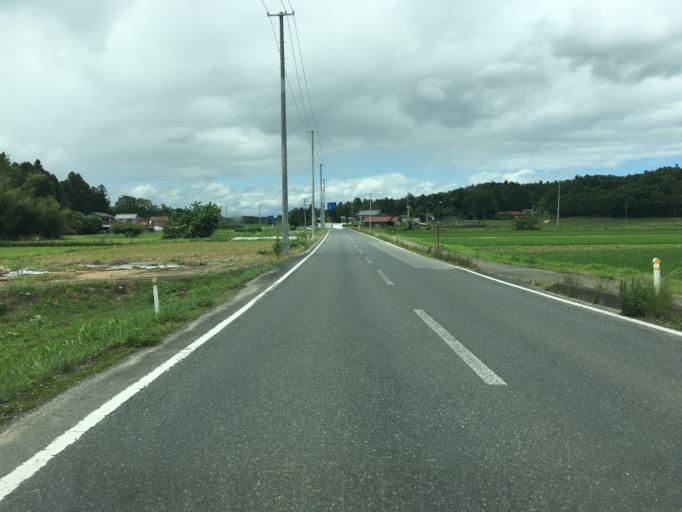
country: JP
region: Miyagi
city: Marumori
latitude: 37.7308
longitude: 140.9287
